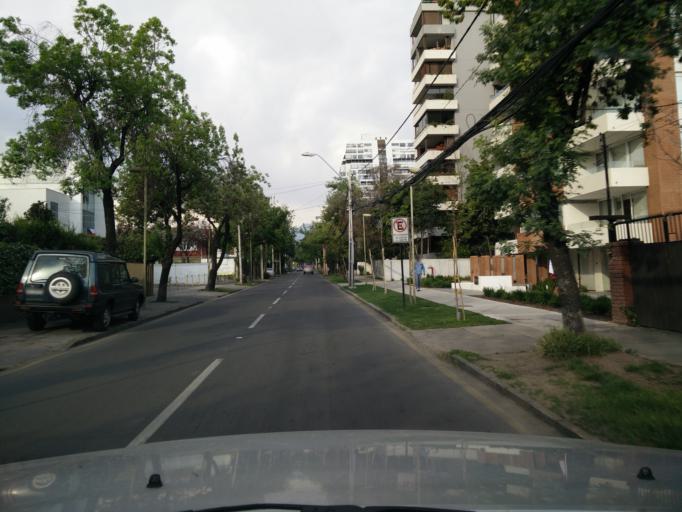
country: CL
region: Santiago Metropolitan
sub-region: Provincia de Santiago
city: Villa Presidente Frei, Nunoa, Santiago, Chile
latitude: -33.4244
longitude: -70.5920
